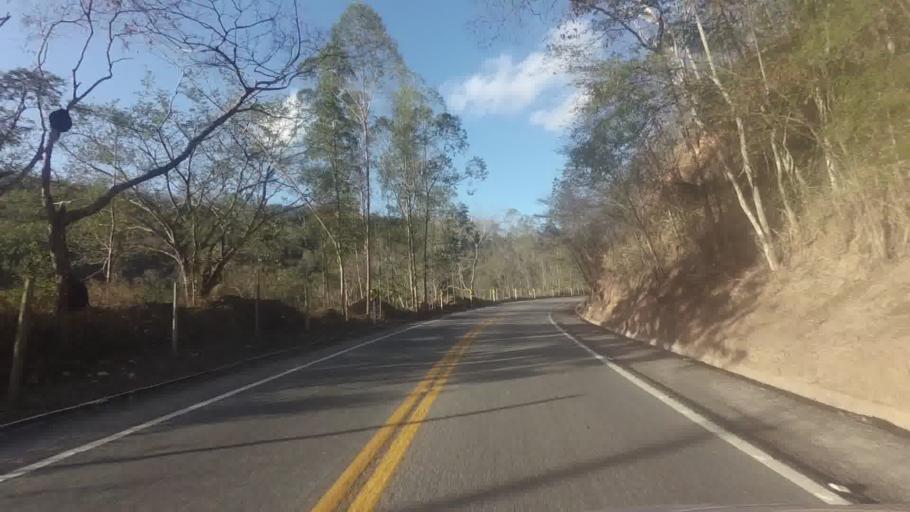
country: BR
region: Espirito Santo
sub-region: Cachoeiro De Itapemirim
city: Cachoeiro de Itapemirim
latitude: -20.8300
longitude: -41.2223
